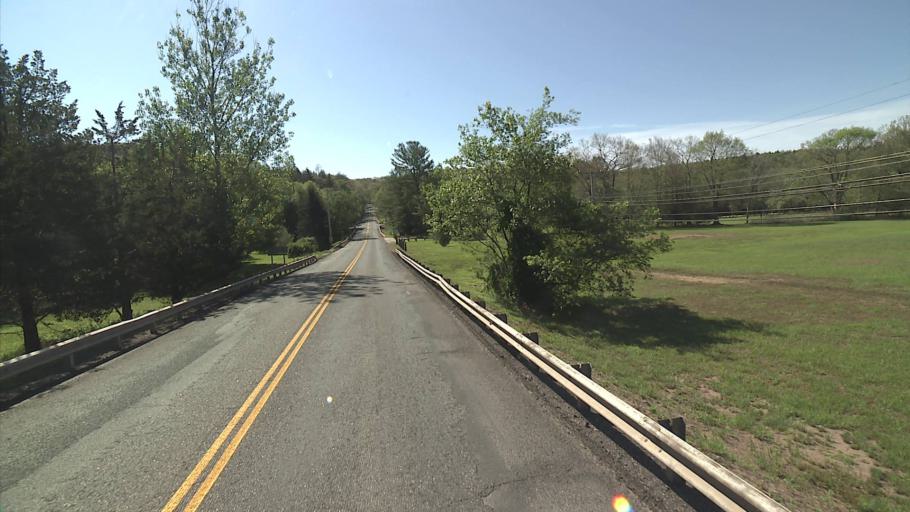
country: US
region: Connecticut
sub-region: Middlesex County
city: Moodus
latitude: 41.5522
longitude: -72.4489
